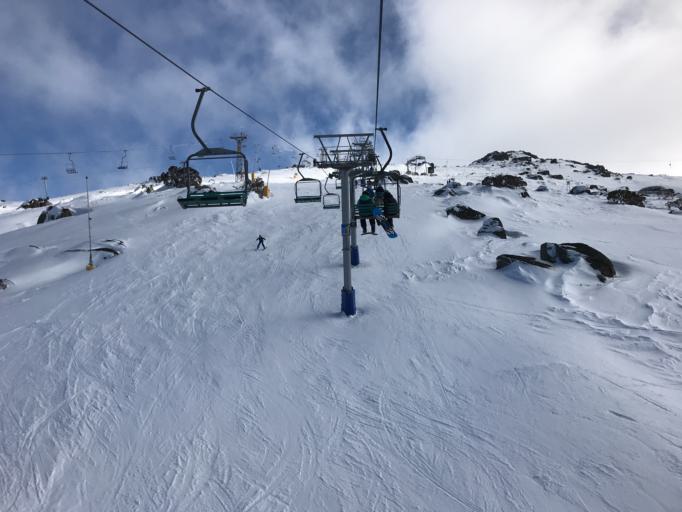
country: AU
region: New South Wales
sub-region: Snowy River
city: Jindabyne
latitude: -36.4096
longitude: 148.3929
